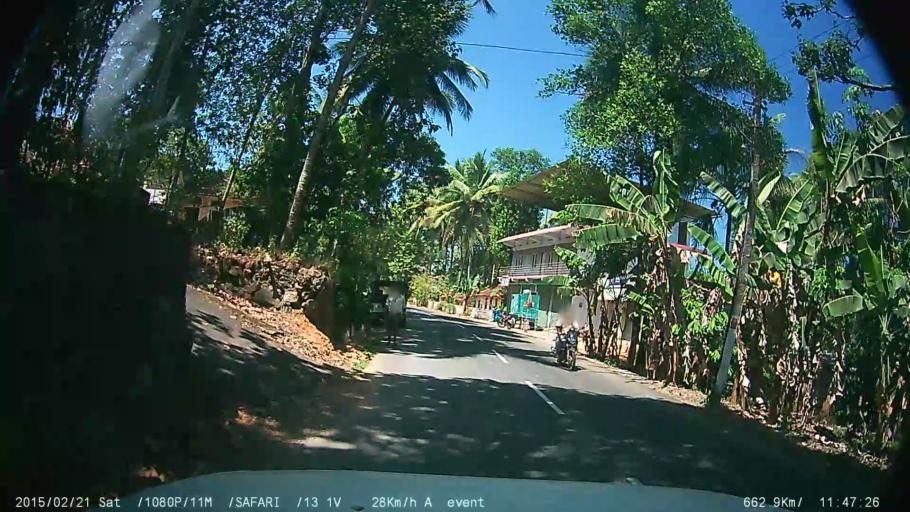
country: IN
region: Kerala
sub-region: Kottayam
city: Lalam
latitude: 9.7749
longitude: 76.7159
